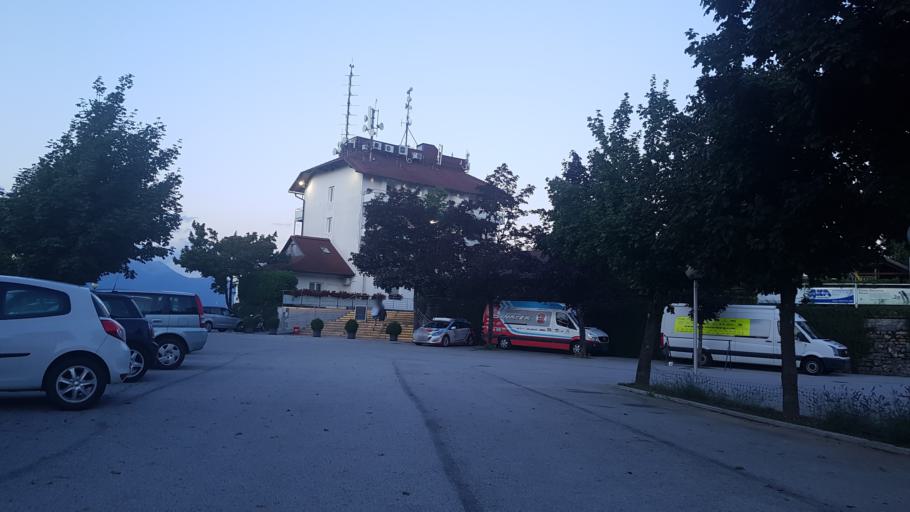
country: SI
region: Kranj
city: Kranj
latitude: 46.2438
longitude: 14.3359
